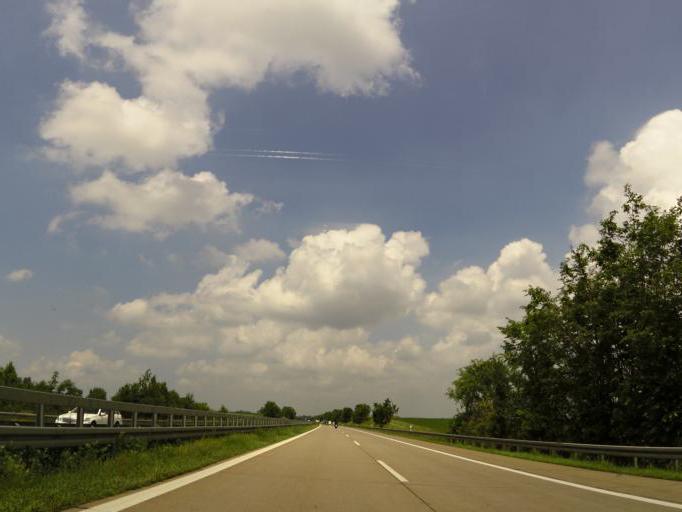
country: DE
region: Baden-Wuerttemberg
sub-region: Regierungsbezirk Stuttgart
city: Westhausen
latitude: 48.9415
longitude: 10.1920
